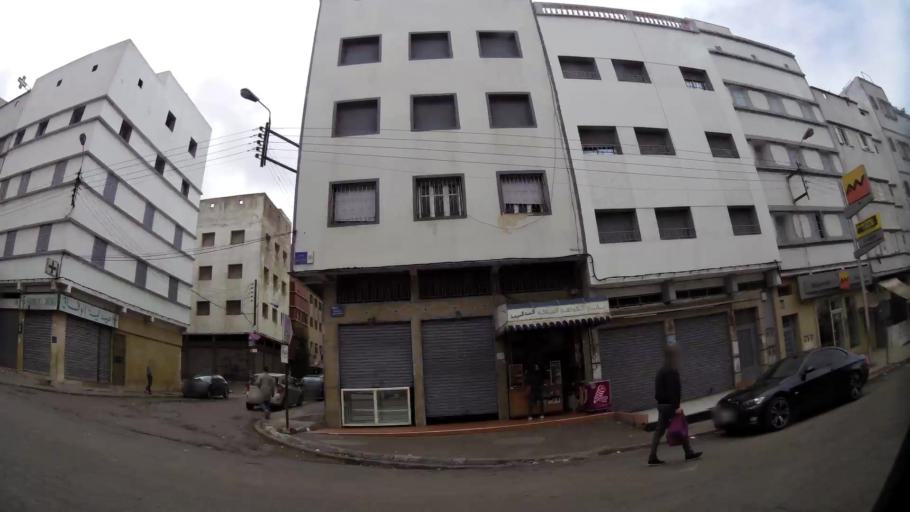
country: MA
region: Grand Casablanca
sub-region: Mediouna
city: Tit Mellil
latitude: 33.6058
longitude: -7.5148
